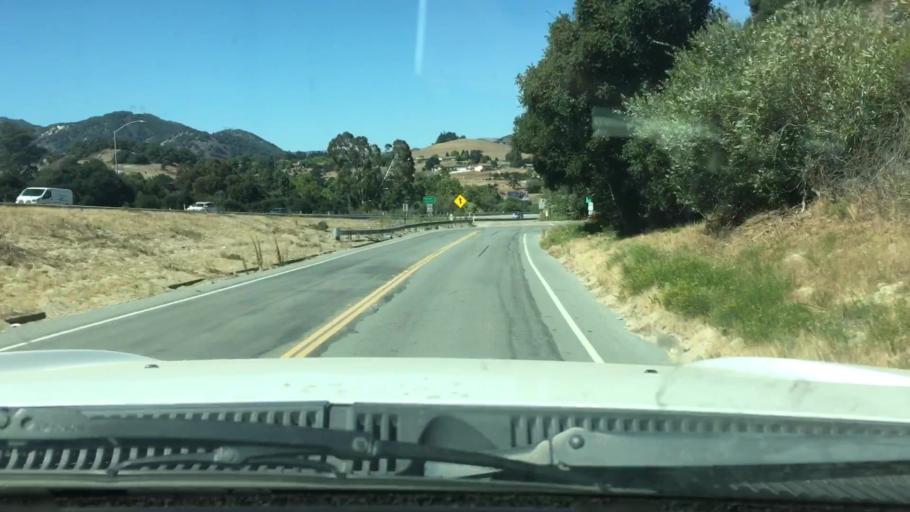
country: US
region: California
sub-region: San Luis Obispo County
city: Avila Beach
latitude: 35.1819
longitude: -120.7007
